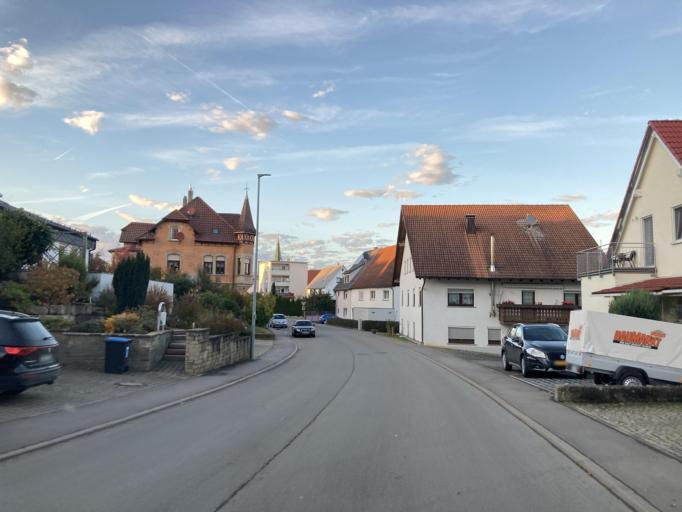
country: DE
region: Baden-Wuerttemberg
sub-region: Regierungsbezirk Stuttgart
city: Bondorf
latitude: 48.4909
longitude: 8.8105
